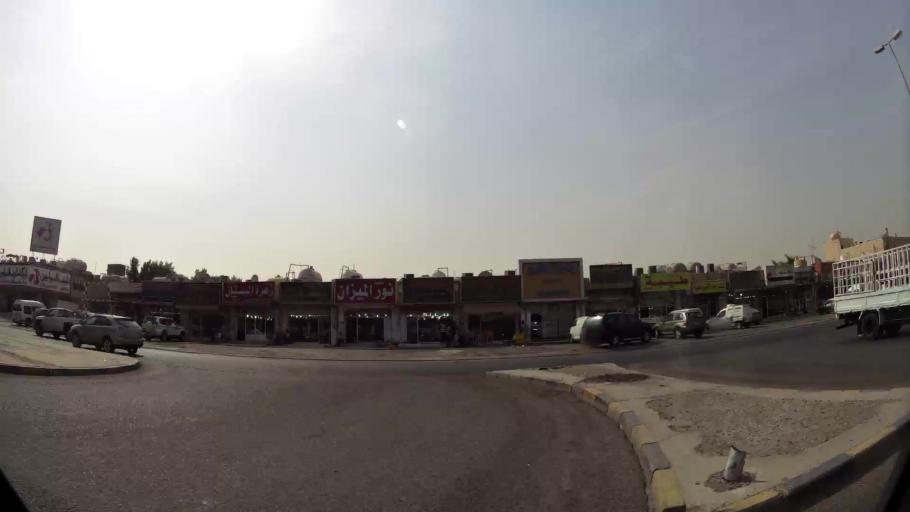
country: KW
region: Al Asimah
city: Ar Rabiyah
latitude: 29.3236
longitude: 47.9294
